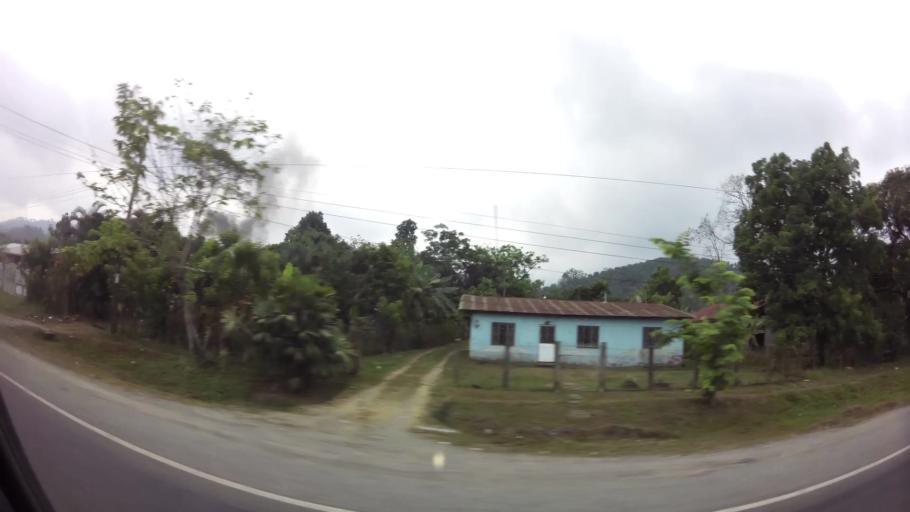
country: HN
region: Yoro
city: Guaimitas
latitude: 15.5000
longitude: -87.7067
